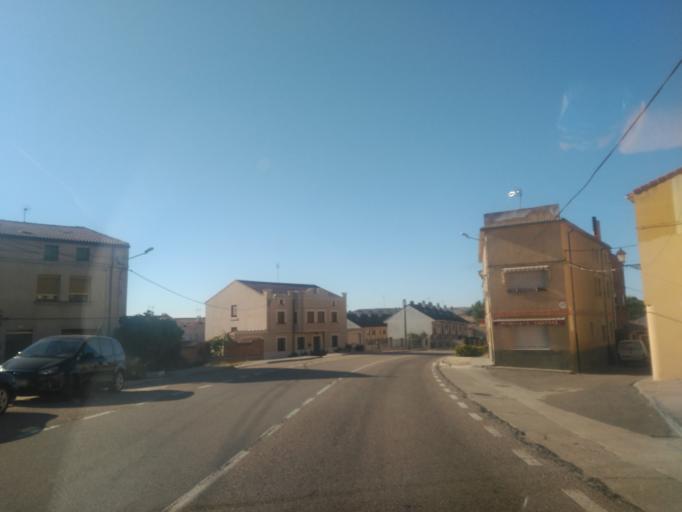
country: ES
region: Castille and Leon
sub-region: Provincia de Burgos
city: Castrillo de la Vega
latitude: 41.6514
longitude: -3.7789
